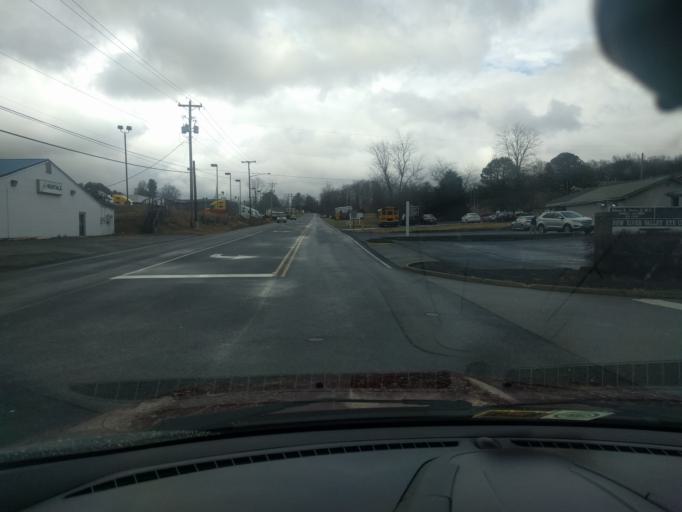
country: US
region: Virginia
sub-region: Pulaski County
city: Pulaski
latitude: 37.0532
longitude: -80.7502
